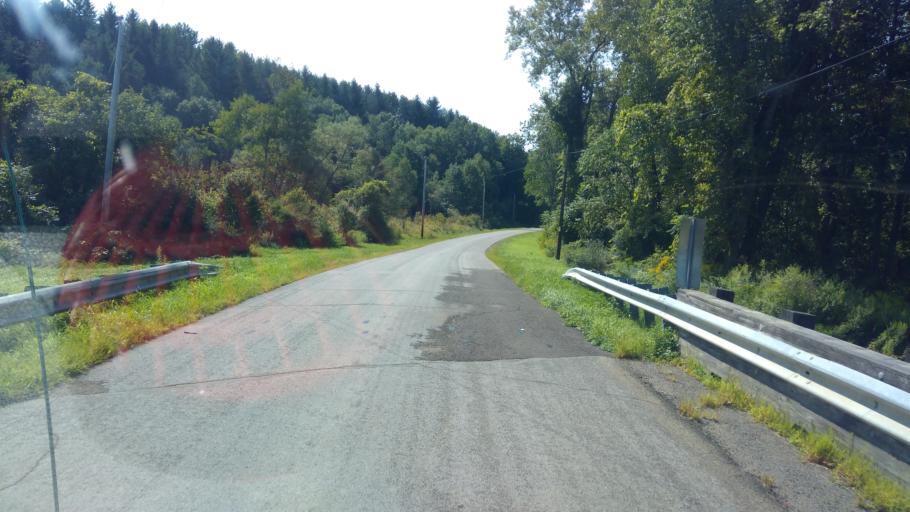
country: US
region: New York
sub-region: Allegany County
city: Belmont
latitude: 42.2452
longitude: -78.0139
